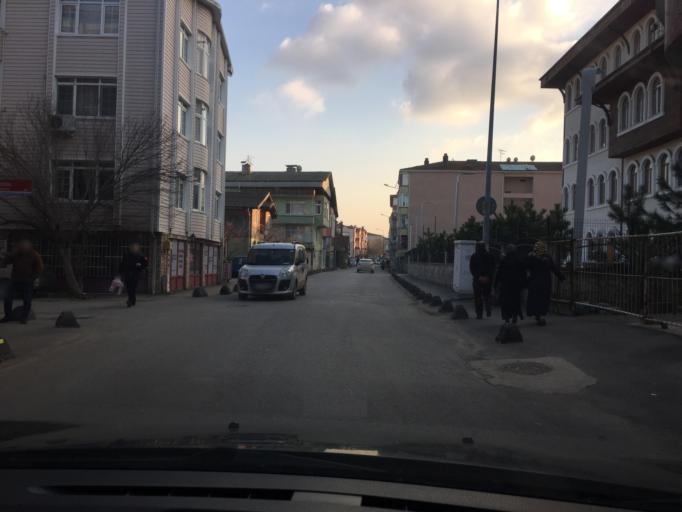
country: TR
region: Sakarya
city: Adapazari
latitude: 40.7834
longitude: 30.4017
